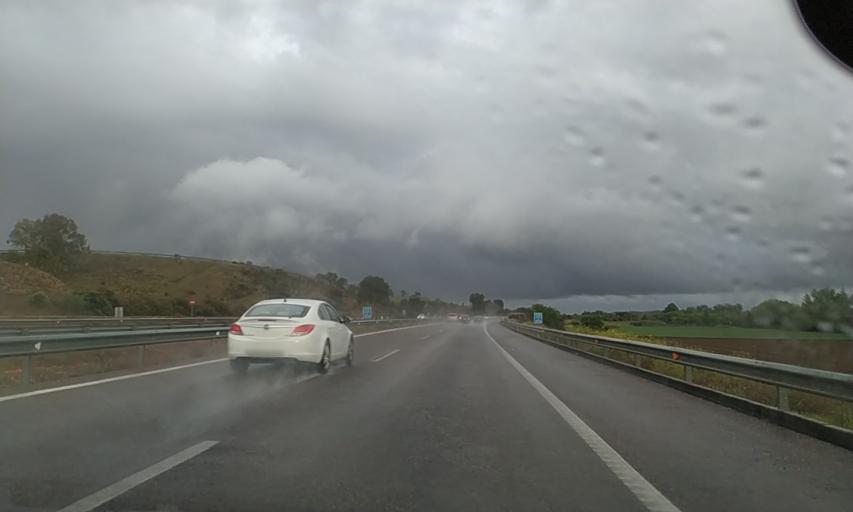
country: ES
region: Extremadura
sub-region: Provincia de Badajoz
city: Valdelacalzada
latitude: 38.8485
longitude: -6.6826
